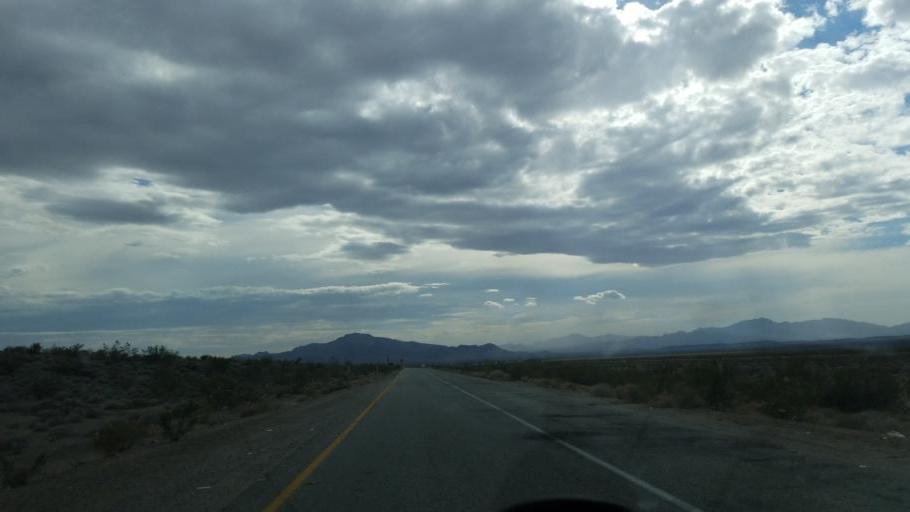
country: US
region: California
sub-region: San Bernardino County
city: Needles
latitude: 34.8130
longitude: -115.1908
